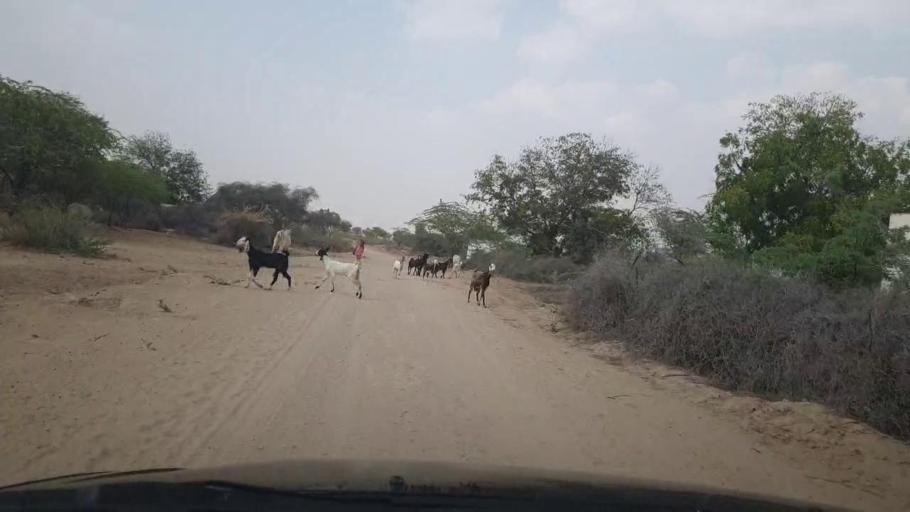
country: PK
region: Sindh
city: Islamkot
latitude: 24.9583
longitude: 70.6321
